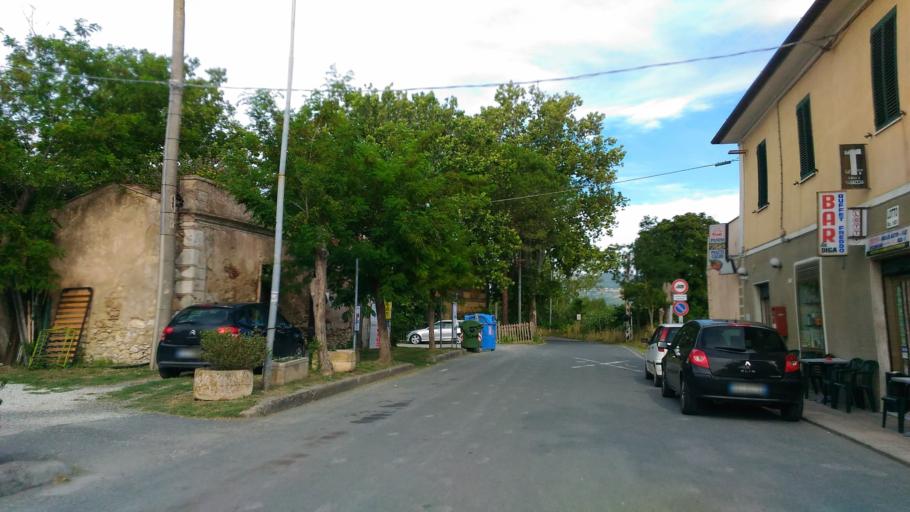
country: IT
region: Tuscany
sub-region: Provincia di Livorno
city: Rosignano Marittimo
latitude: 43.4373
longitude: 10.4886
